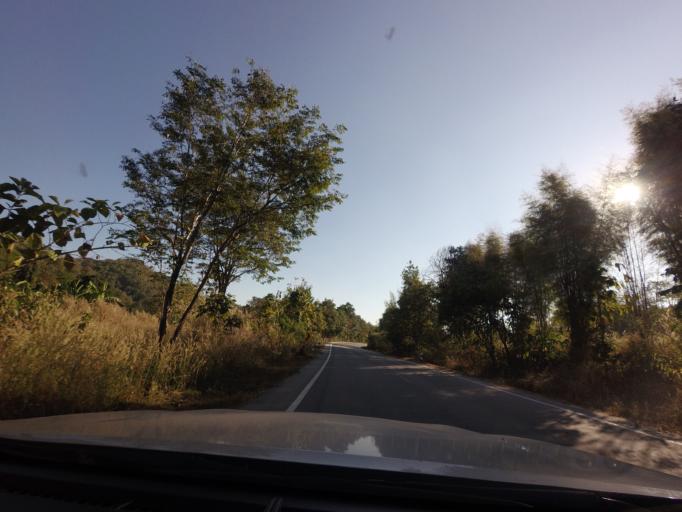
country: TH
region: Lampang
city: Chae Hom
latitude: 18.5684
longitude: 99.6249
